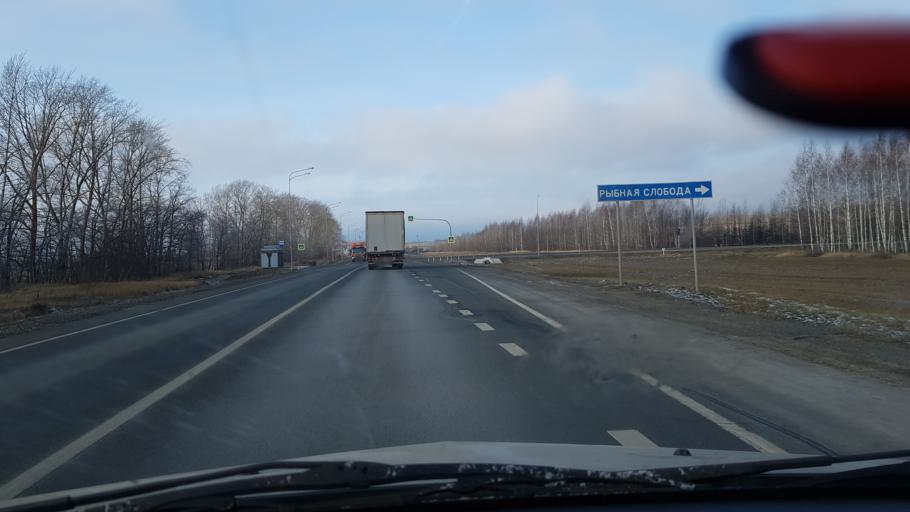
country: RU
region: Tatarstan
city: Laishevo
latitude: 55.3904
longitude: 49.8139
